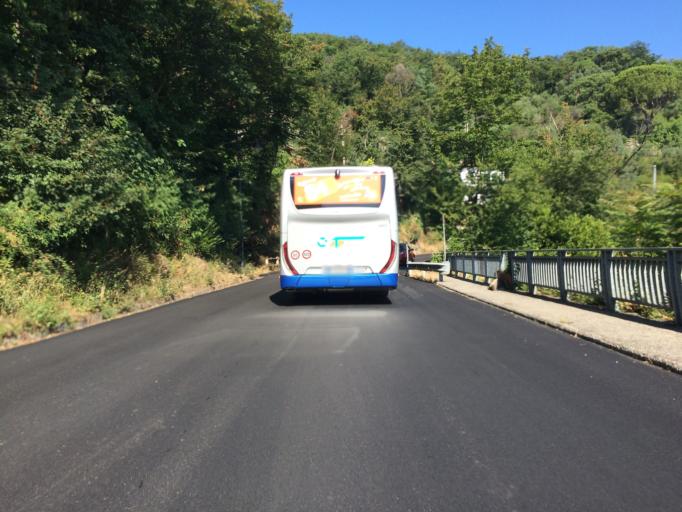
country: IT
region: Liguria
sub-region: Provincia di Genova
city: Camogli
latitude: 44.3393
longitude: 9.1826
